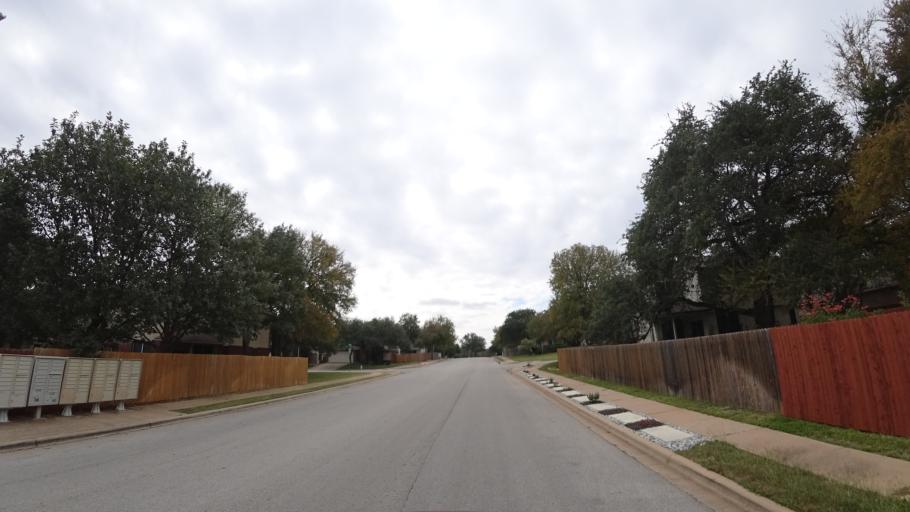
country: US
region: Texas
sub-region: Travis County
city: Wells Branch
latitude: 30.4288
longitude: -97.7172
